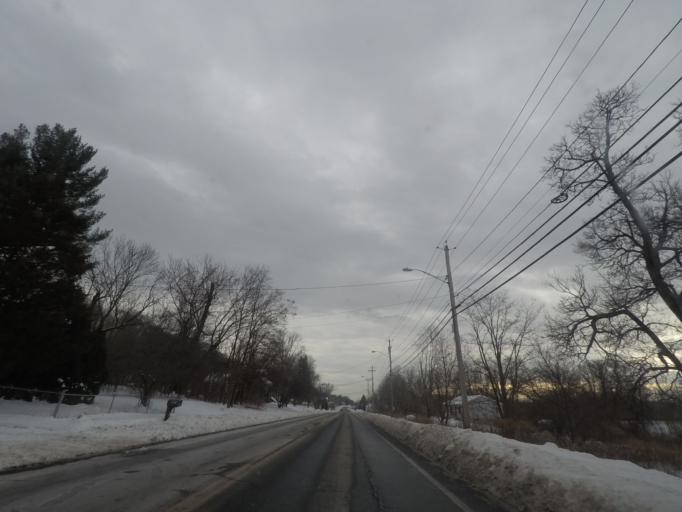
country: US
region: New York
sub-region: Rensselaer County
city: Rensselaer
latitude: 42.6261
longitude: -73.7444
